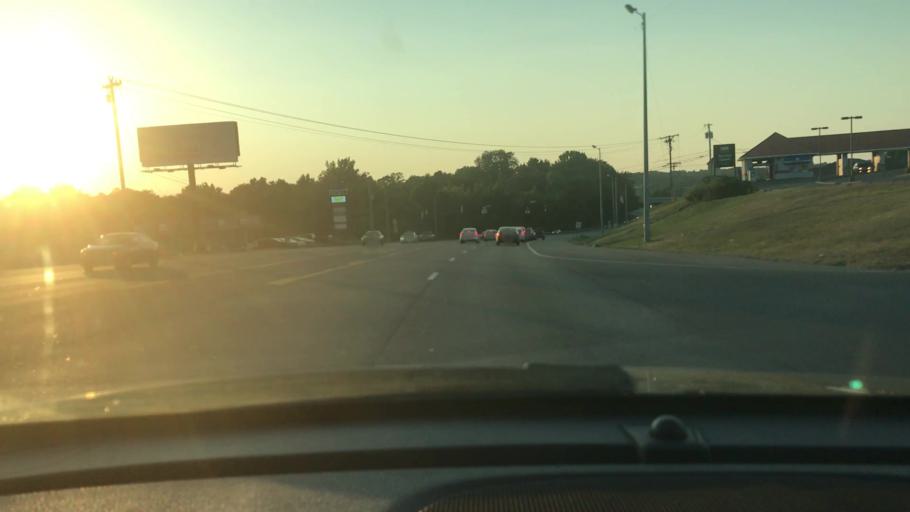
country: US
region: Tennessee
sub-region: Dickson County
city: Dickson
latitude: 36.0784
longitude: -87.3767
